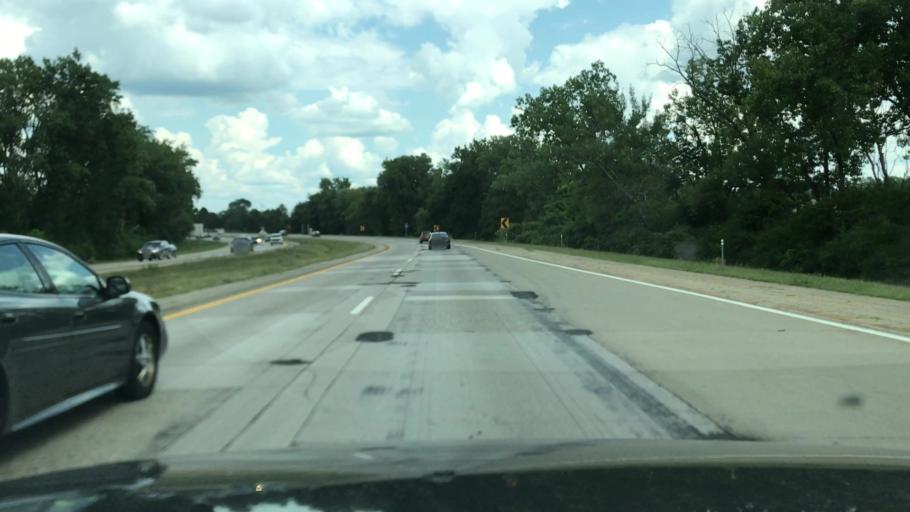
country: US
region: Michigan
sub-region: Kent County
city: Grand Rapids
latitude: 42.9733
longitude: -85.6352
